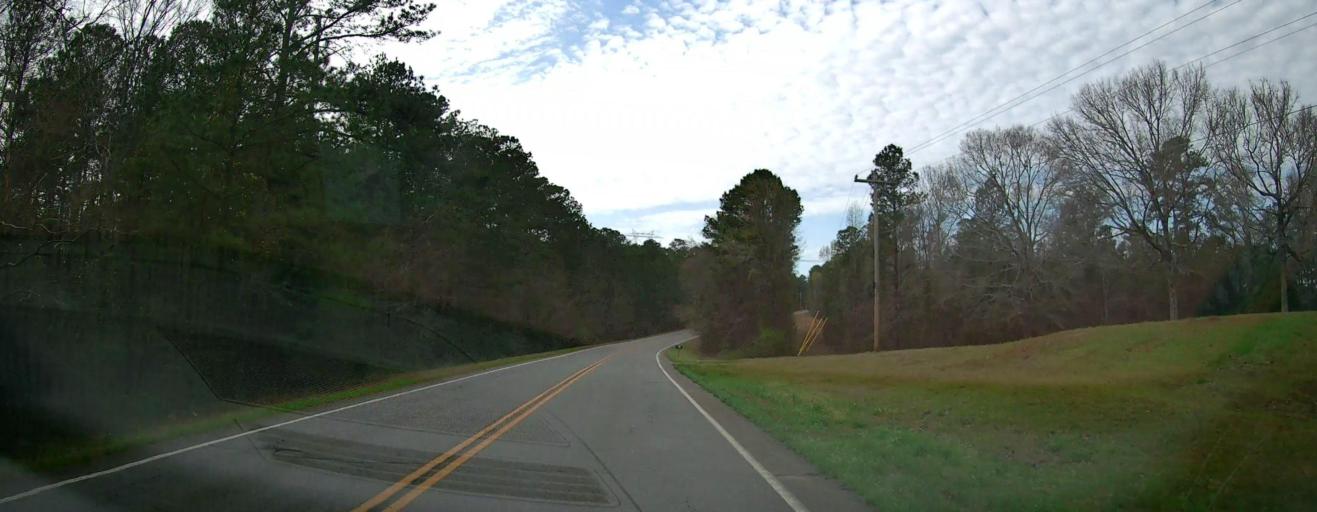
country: US
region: Georgia
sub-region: Jones County
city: Gray
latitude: 32.9830
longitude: -83.6686
